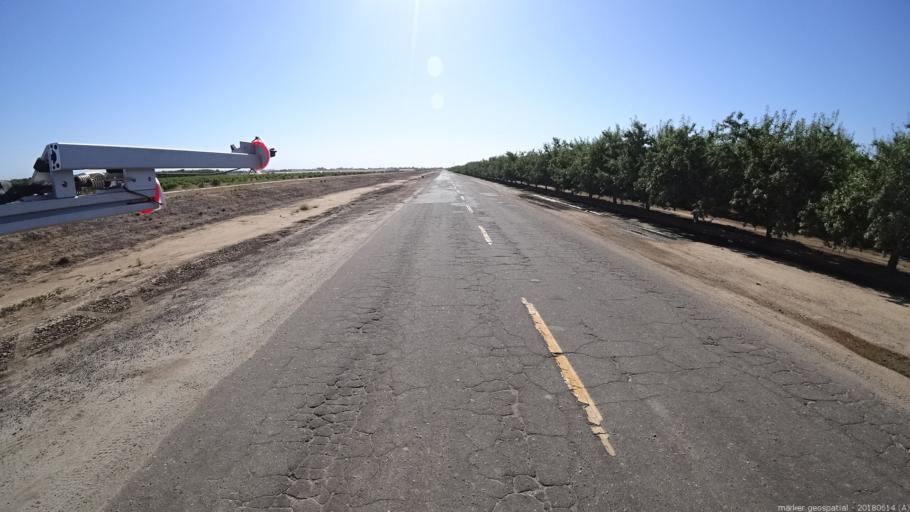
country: US
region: California
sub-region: Madera County
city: Madera
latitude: 36.9819
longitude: -120.1238
